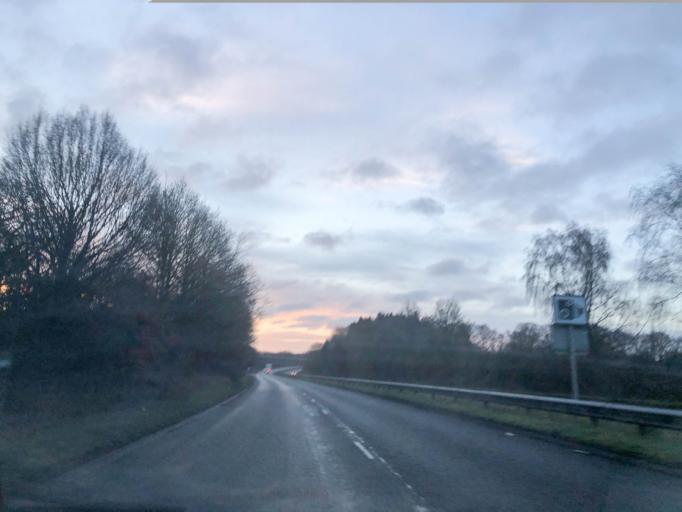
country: GB
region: England
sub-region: Solihull
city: Tidbury Green
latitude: 52.3819
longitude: -1.8936
